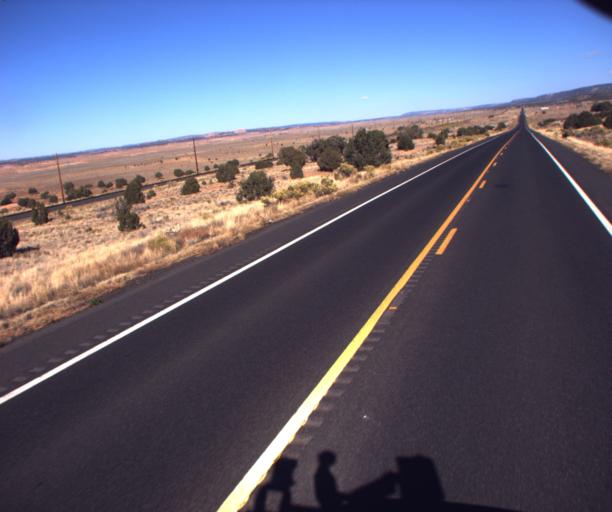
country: US
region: Arizona
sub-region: Coconino County
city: Kaibito
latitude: 36.4515
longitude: -110.7149
